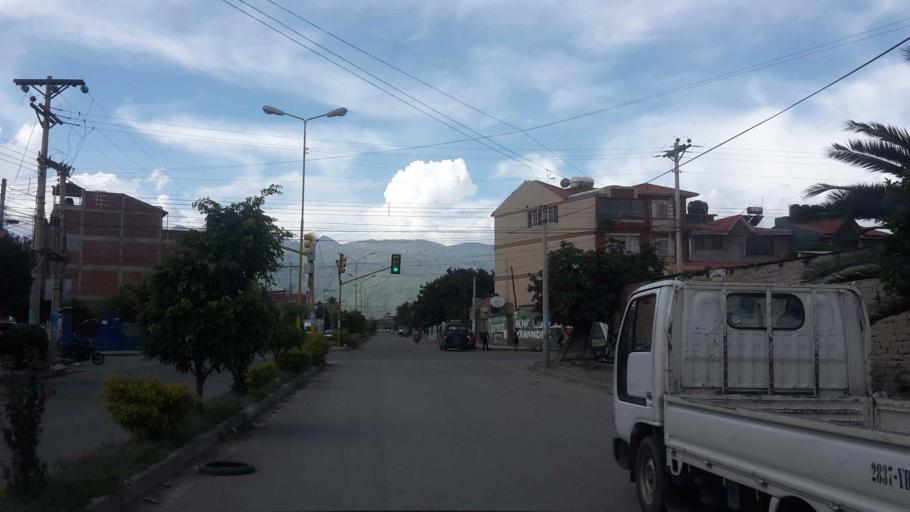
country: BO
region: Cochabamba
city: Cochabamba
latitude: -17.3990
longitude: -66.2738
